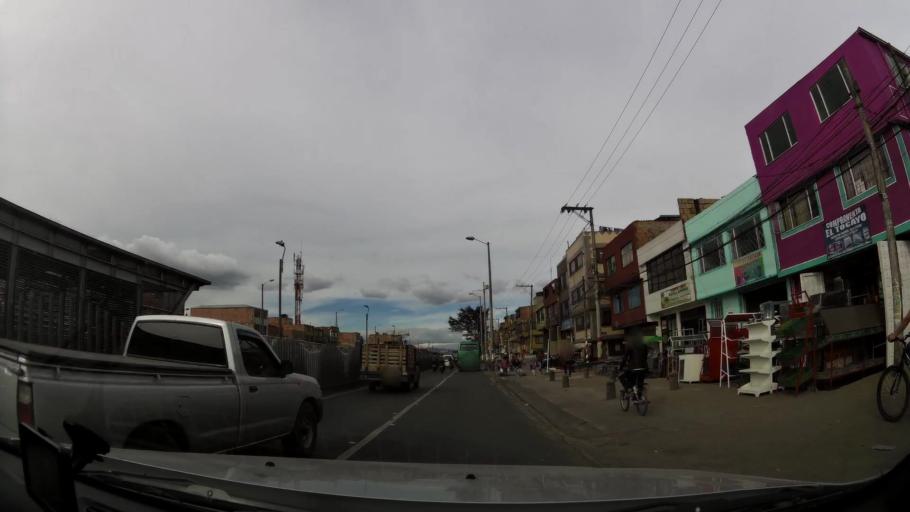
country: CO
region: Cundinamarca
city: Soacha
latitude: 4.6328
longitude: -74.1648
